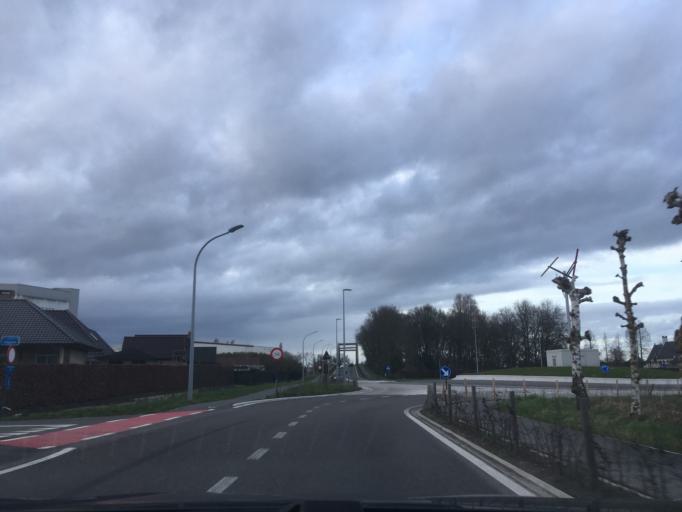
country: BE
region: Flanders
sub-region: Provincie West-Vlaanderen
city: Oostrozebeke
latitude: 50.9039
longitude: 3.3263
